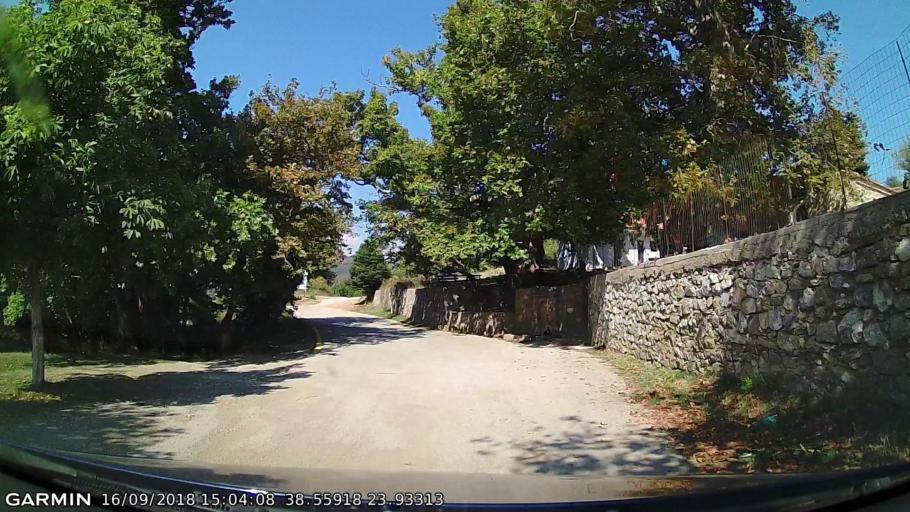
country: GR
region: Central Greece
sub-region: Nomos Evvoias
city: Yimnon
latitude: 38.5592
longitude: 23.9332
